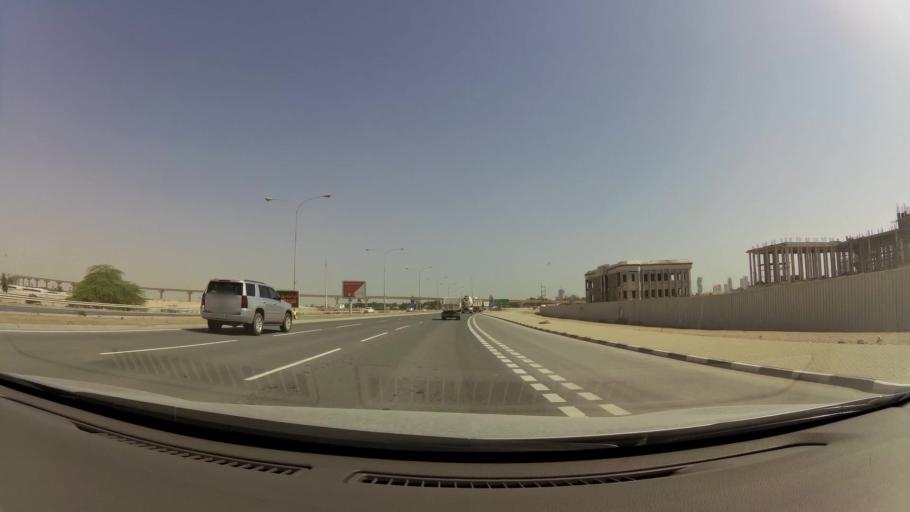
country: QA
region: Baladiyat ad Dawhah
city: Doha
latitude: 25.3746
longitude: 51.4979
